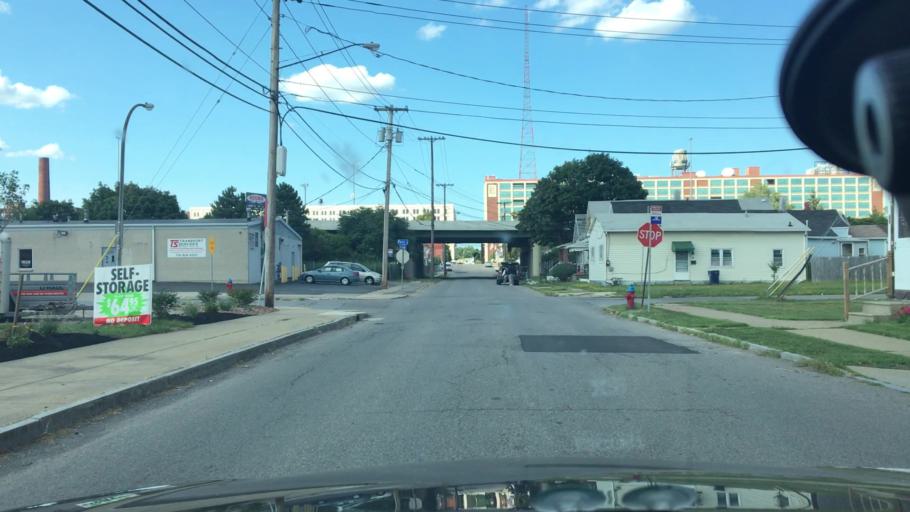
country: US
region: New York
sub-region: Erie County
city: Buffalo
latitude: 42.8713
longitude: -78.8520
